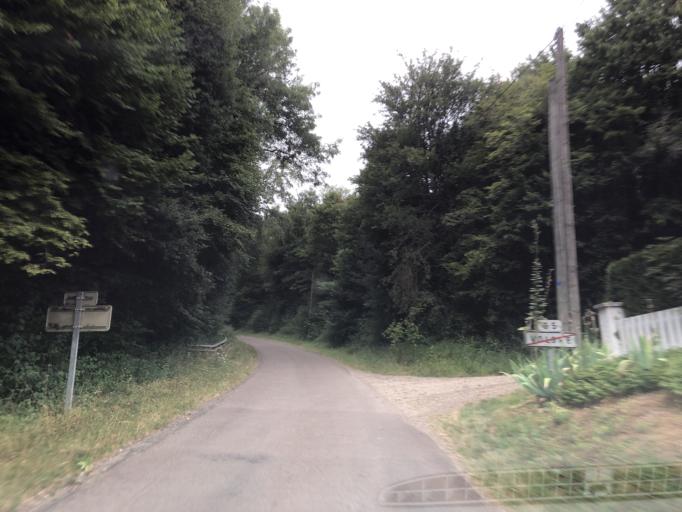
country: FR
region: Bourgogne
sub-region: Departement de l'Yonne
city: Aillant-sur-Tholon
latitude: 47.9185
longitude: 3.3218
